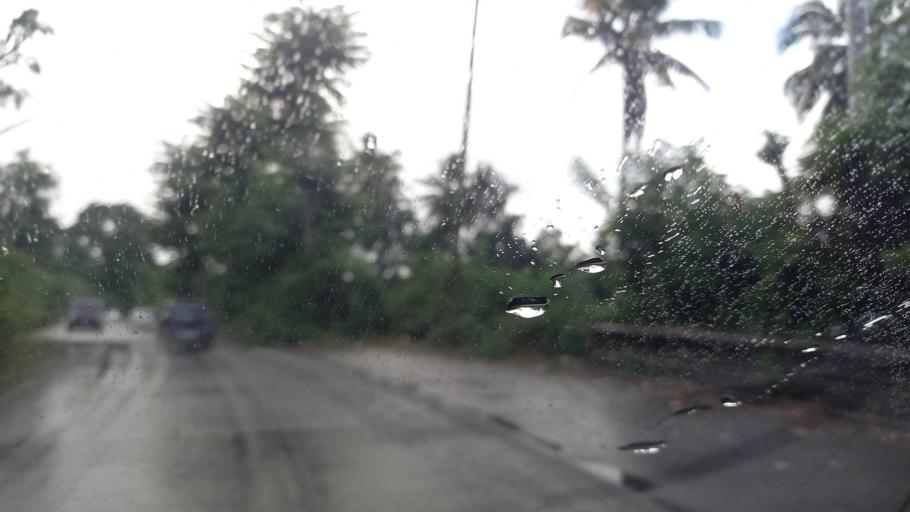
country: YT
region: Ouangani
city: Ouangani
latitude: -12.8358
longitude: 45.1477
